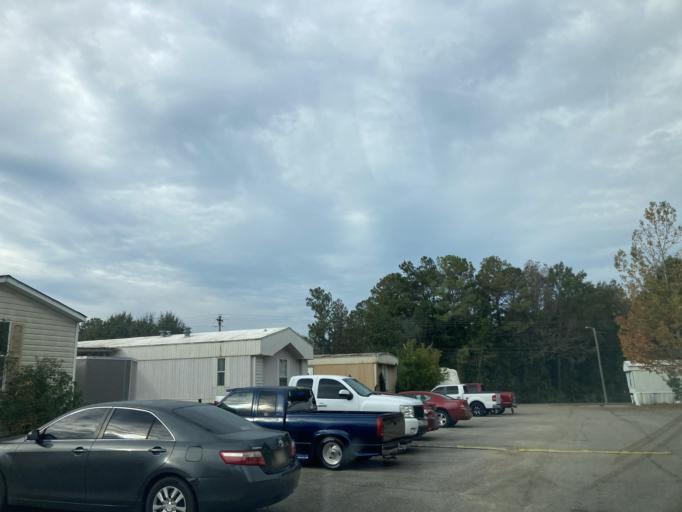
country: US
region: Mississippi
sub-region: Lamar County
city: West Hattiesburg
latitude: 31.3075
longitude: -89.3795
